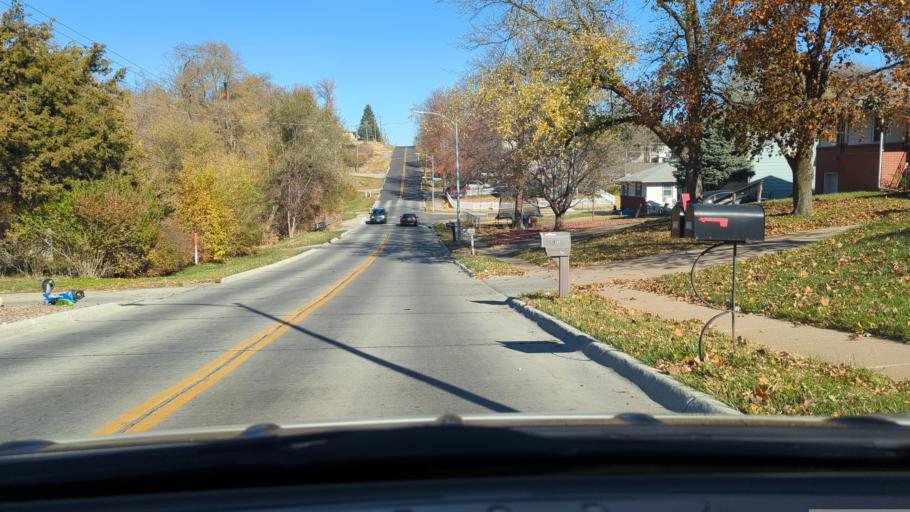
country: US
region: Nebraska
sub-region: Sarpy County
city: La Vista
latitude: 41.1874
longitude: -95.9770
